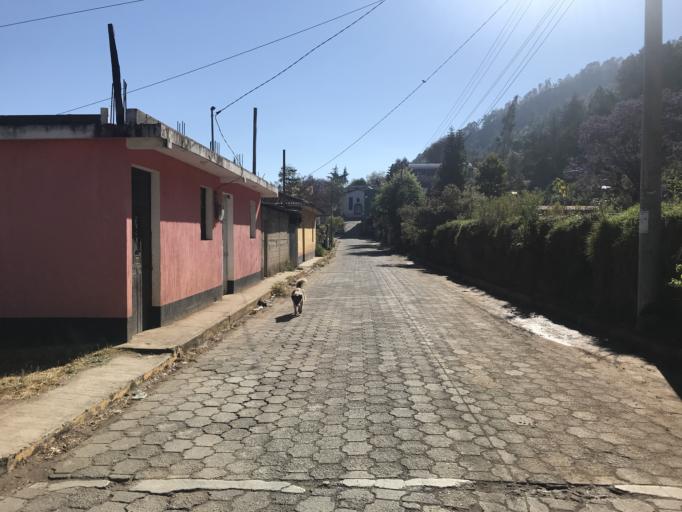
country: GT
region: San Marcos
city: San Miguel Ixtahuacan
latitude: 15.2722
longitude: -91.7464
